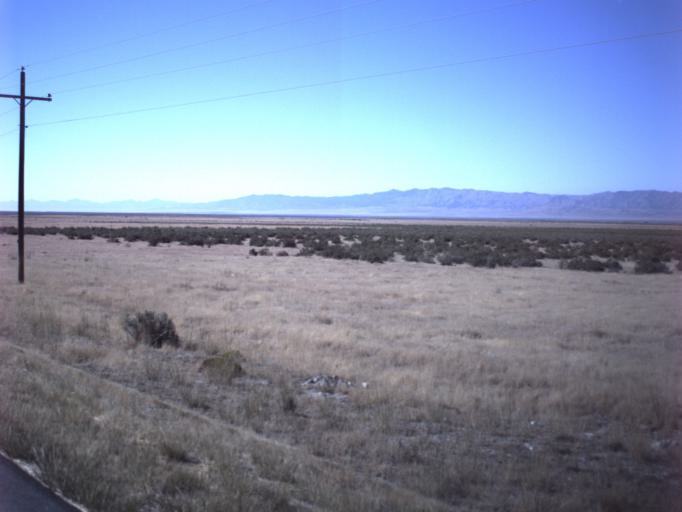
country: US
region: Utah
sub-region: Tooele County
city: Grantsville
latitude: 40.6971
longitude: -112.6667
